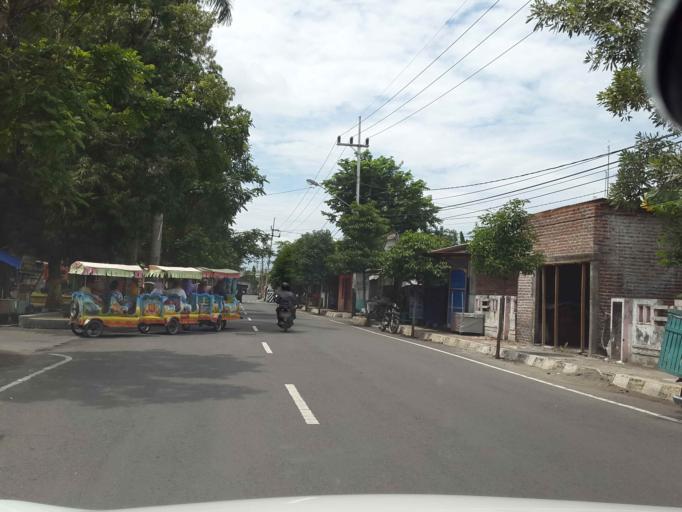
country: ID
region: East Java
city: Mojokerto
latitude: -7.4579
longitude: 112.4428
